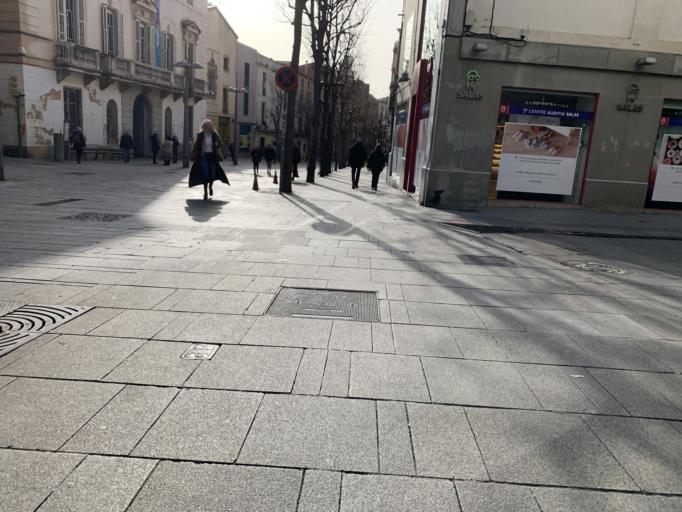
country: ES
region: Catalonia
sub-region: Provincia de Barcelona
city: Mataro
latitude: 41.5401
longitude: 2.4445
